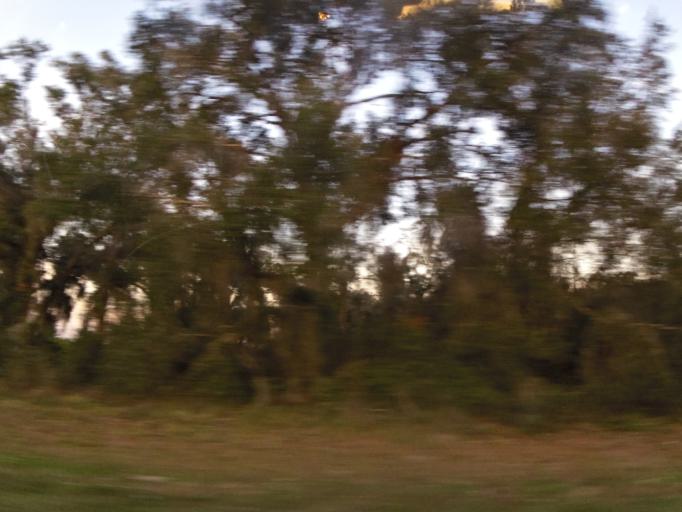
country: US
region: Florida
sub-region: Volusia County
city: De Leon Springs
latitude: 29.1568
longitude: -81.2948
